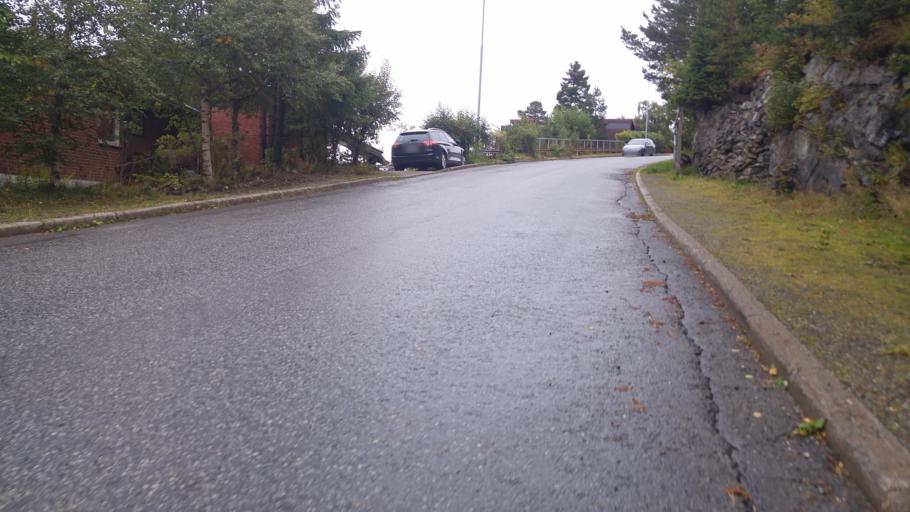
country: NO
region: Sor-Trondelag
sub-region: Trondheim
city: Trondheim
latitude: 63.4525
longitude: 10.3015
